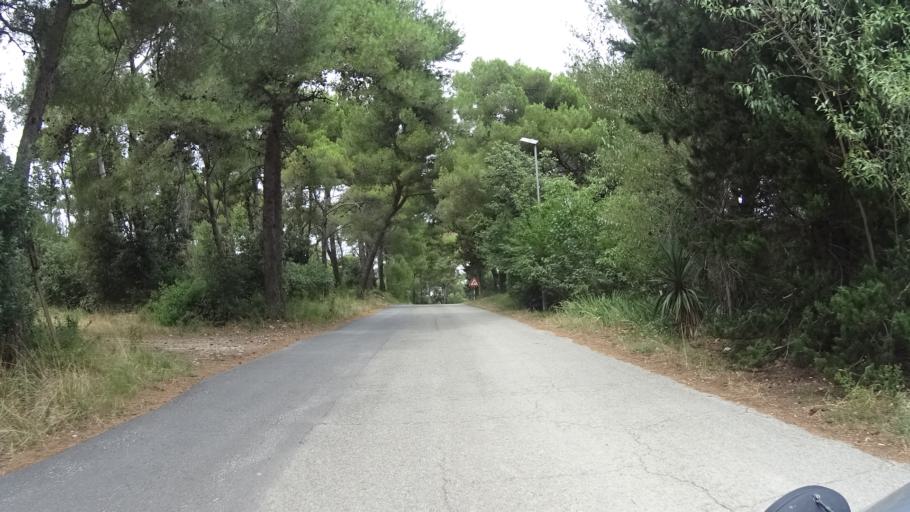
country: HR
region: Istarska
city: Medulin
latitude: 44.8039
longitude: 13.9070
